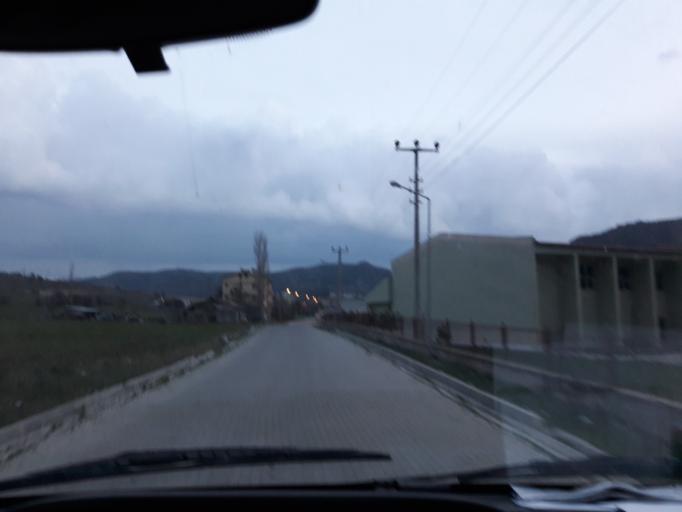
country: TR
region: Giresun
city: Alucra
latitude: 40.3240
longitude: 38.7709
